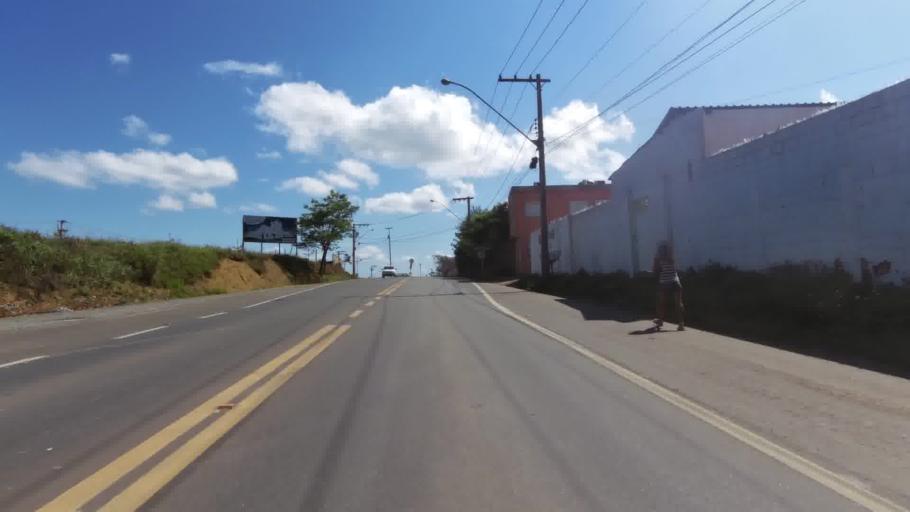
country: BR
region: Espirito Santo
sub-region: Piuma
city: Piuma
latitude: -20.8209
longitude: -40.6264
